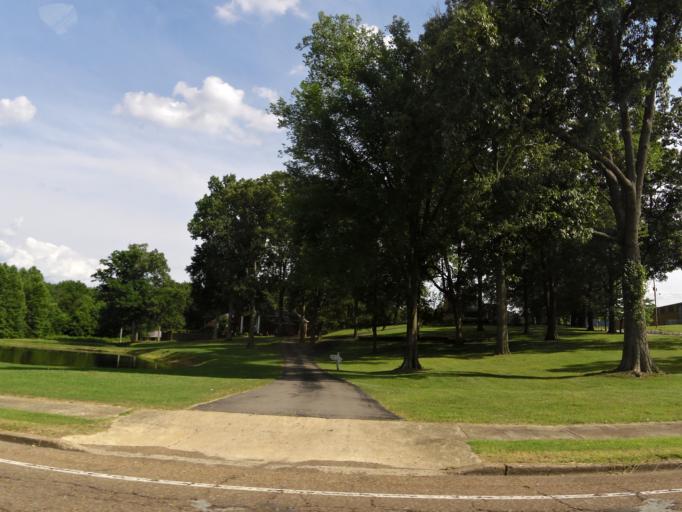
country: US
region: Tennessee
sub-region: Carroll County
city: Bruceton
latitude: 36.0352
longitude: -88.2606
